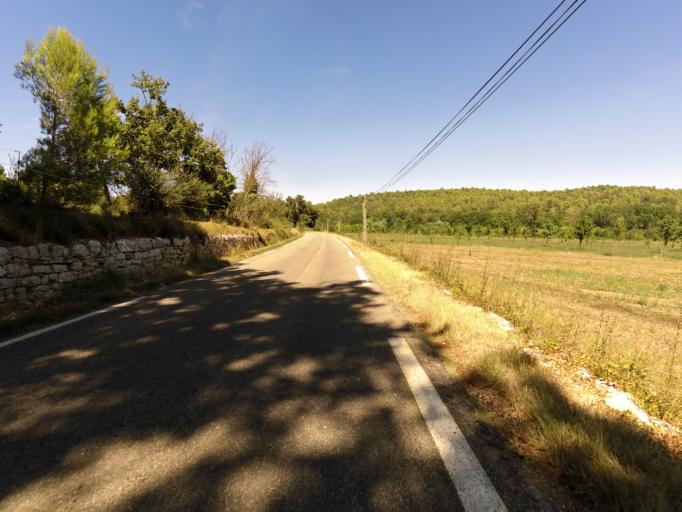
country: FR
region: Languedoc-Roussillon
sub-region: Departement du Gard
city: Sommieres
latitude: 43.8161
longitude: 4.0682
